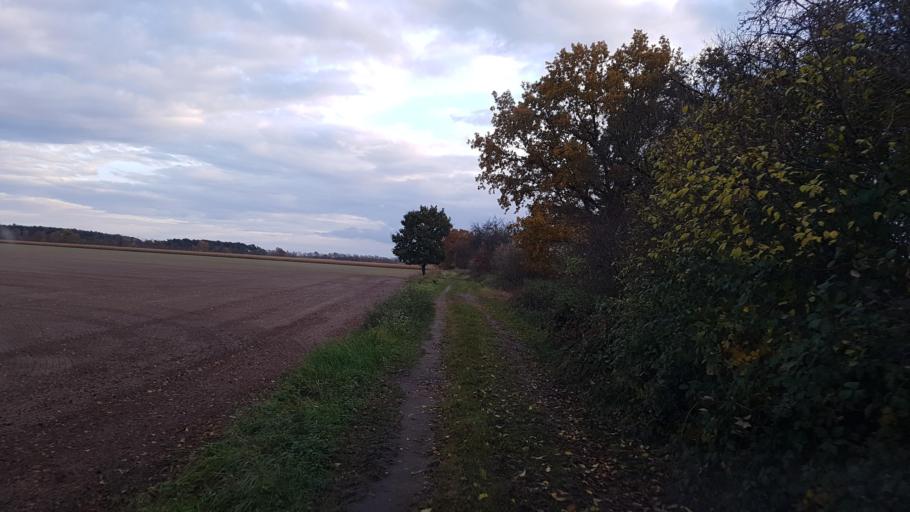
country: DE
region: Saxony-Anhalt
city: Seyda
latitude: 51.9394
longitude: 12.8755
